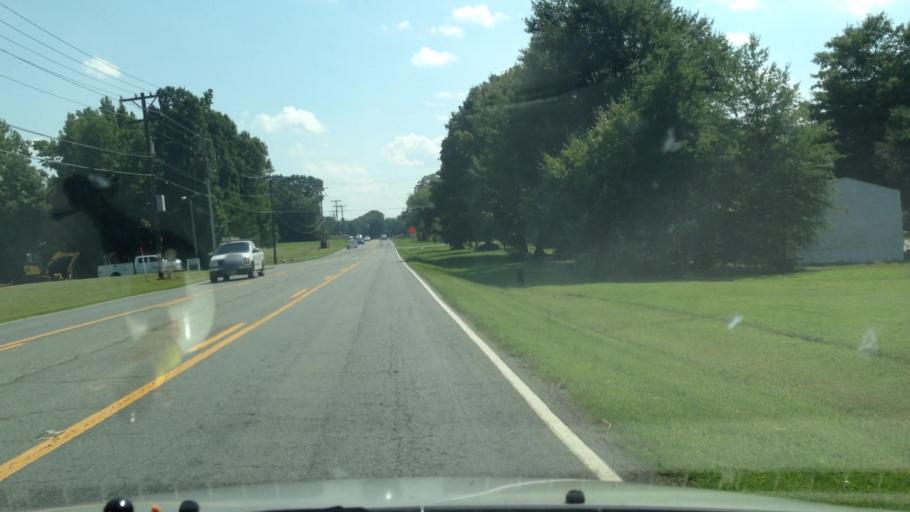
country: US
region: North Carolina
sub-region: Forsyth County
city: Kernersville
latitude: 36.1394
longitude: -80.0505
